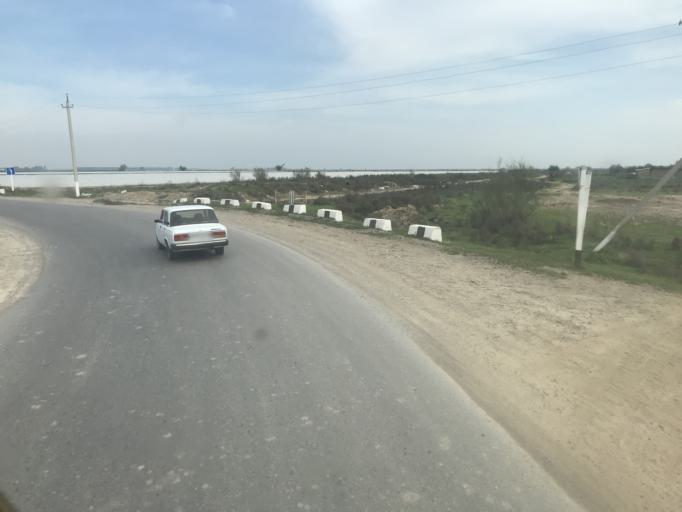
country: KZ
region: Ongtustik Qazaqstan
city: Asykata
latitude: 40.9838
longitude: 68.2970
